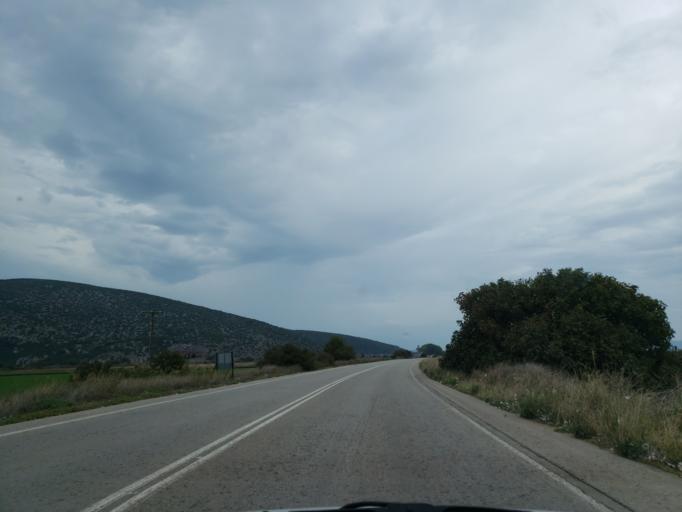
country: GR
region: Central Greece
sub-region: Nomos Voiotias
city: Orchomenos
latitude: 38.4894
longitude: 23.0632
